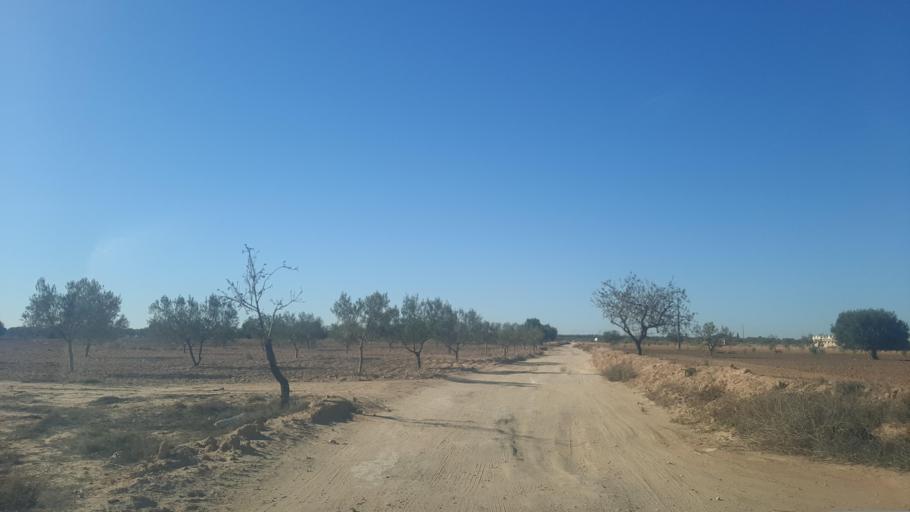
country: TN
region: Safaqis
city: Sfax
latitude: 34.8867
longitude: 10.5862
